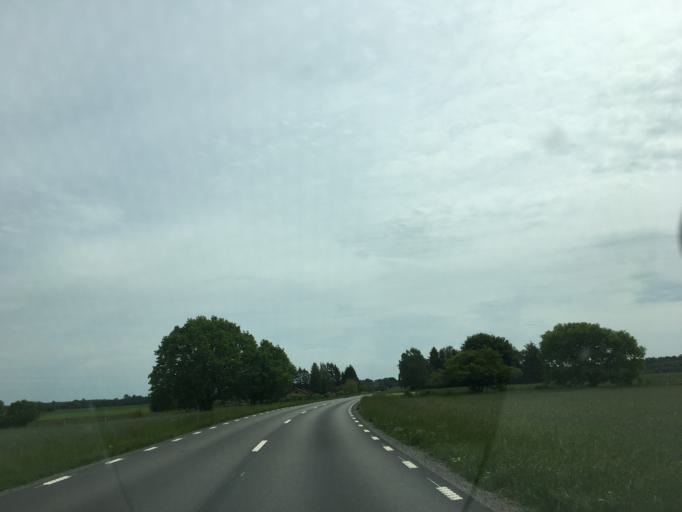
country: SE
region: Skane
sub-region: Sjobo Kommun
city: Blentarp
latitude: 55.6055
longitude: 13.5836
